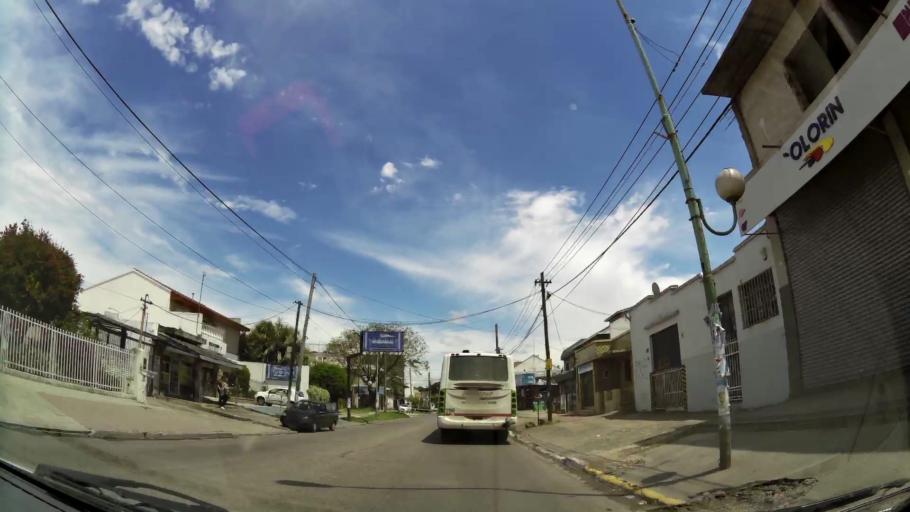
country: AR
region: Buenos Aires
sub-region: Partido de Quilmes
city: Quilmes
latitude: -34.7833
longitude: -58.2672
